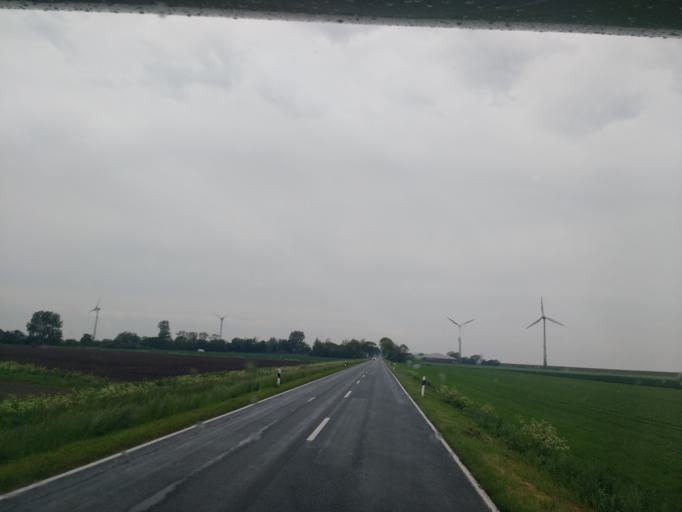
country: DE
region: Lower Saxony
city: Werdum
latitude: 53.6923
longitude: 7.7635
